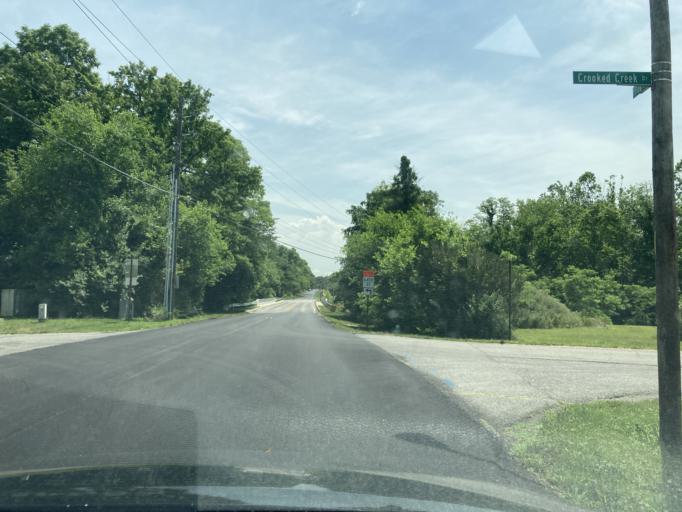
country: US
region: Indiana
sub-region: Marion County
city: Meridian Hills
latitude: 39.8647
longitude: -86.1905
